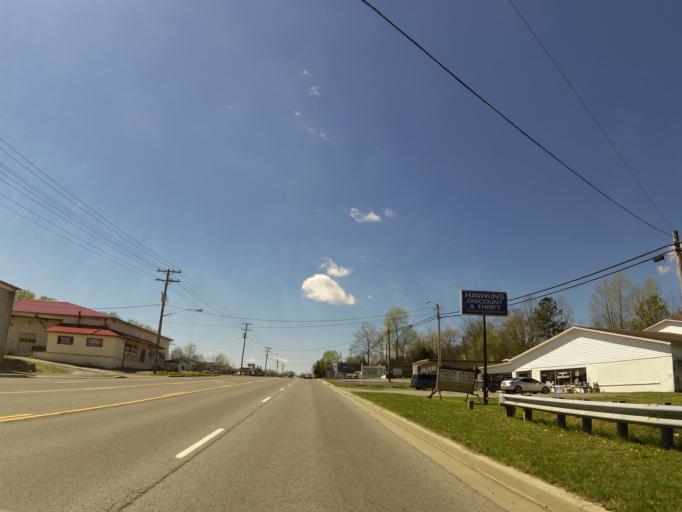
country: US
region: Tennessee
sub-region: DeKalb County
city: Smithville
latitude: 35.9577
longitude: -85.8055
